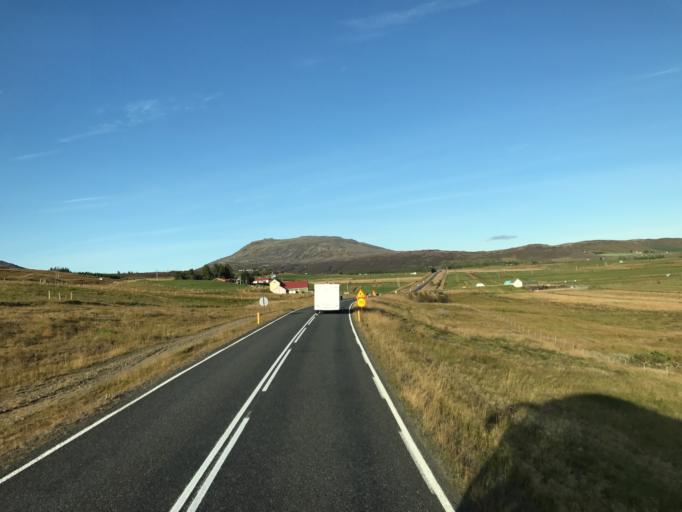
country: IS
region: South
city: Selfoss
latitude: 64.2661
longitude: -20.4654
